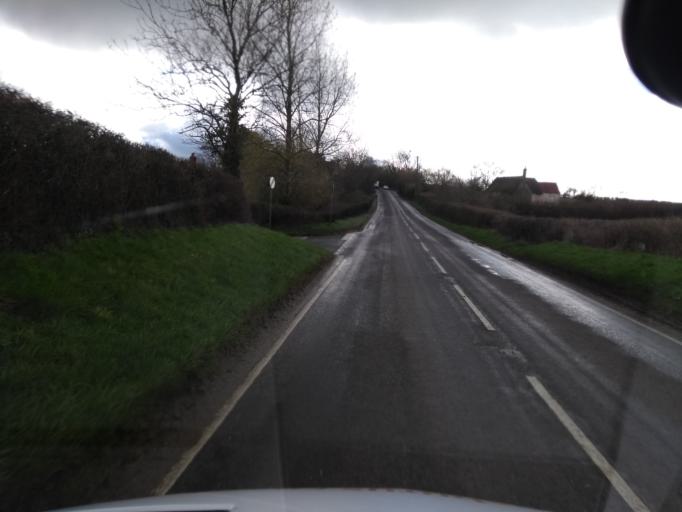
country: GB
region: England
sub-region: Dorset
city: Sherborne
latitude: 50.9291
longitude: -2.4934
